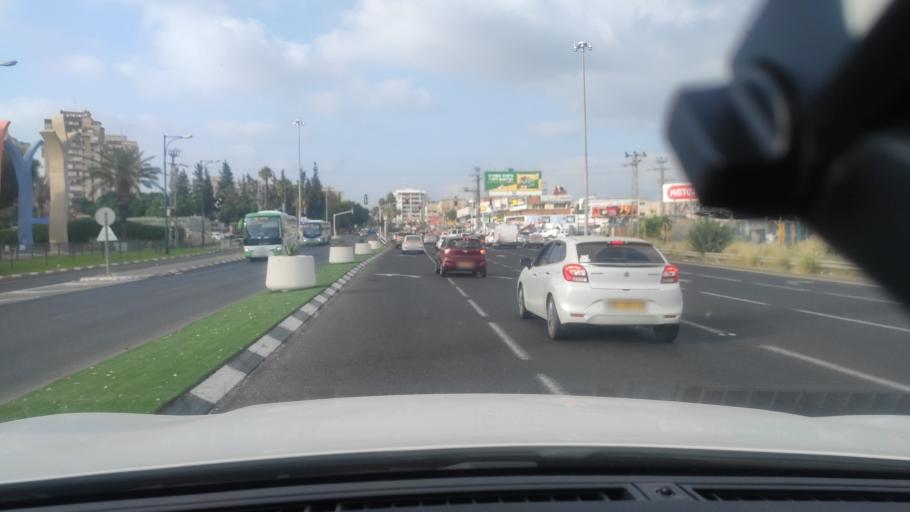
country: IL
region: Central District
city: Petah Tiqwa
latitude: 32.1031
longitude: 34.8984
